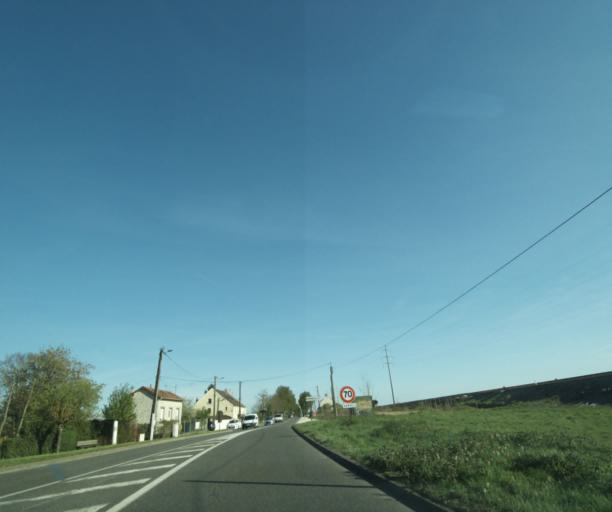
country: FR
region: Ile-de-France
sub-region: Departement de Seine-et-Marne
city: Bailly-Carrois
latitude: 48.5767
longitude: 2.9921
